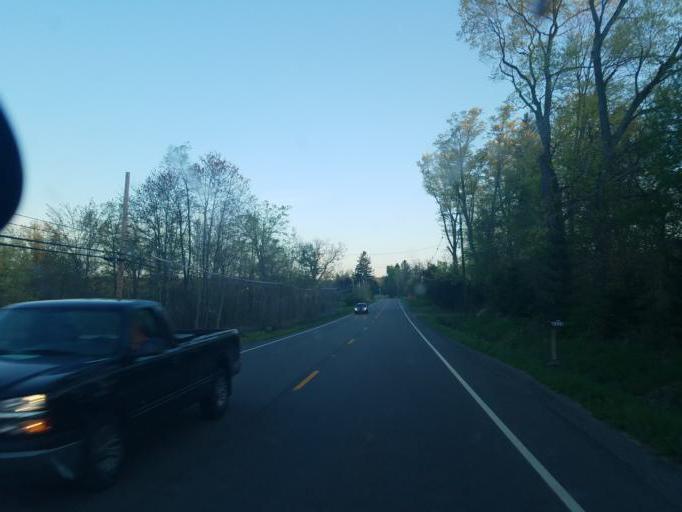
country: US
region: Ohio
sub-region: Trumbull County
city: Brookfield Center
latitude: 41.3407
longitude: -80.5697
